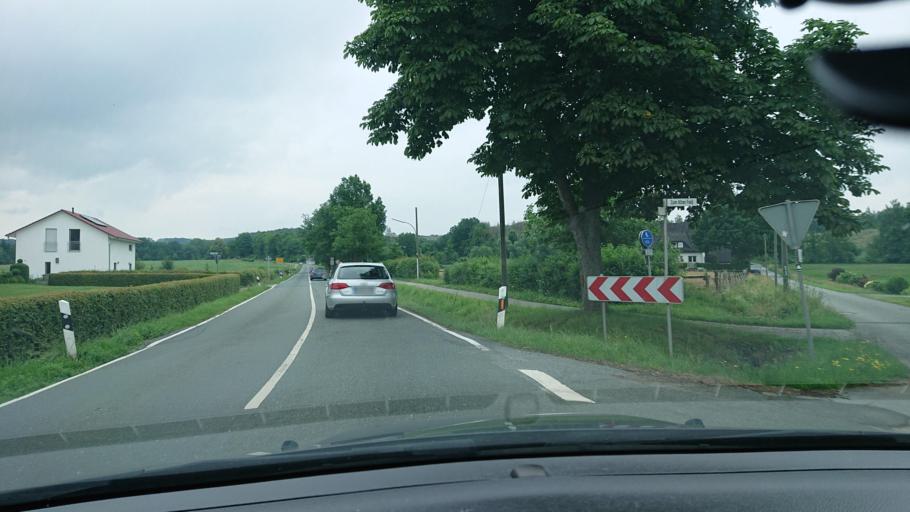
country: DE
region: North Rhine-Westphalia
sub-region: Regierungsbezirk Arnsberg
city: Mohnesee
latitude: 51.4748
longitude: 8.2263
